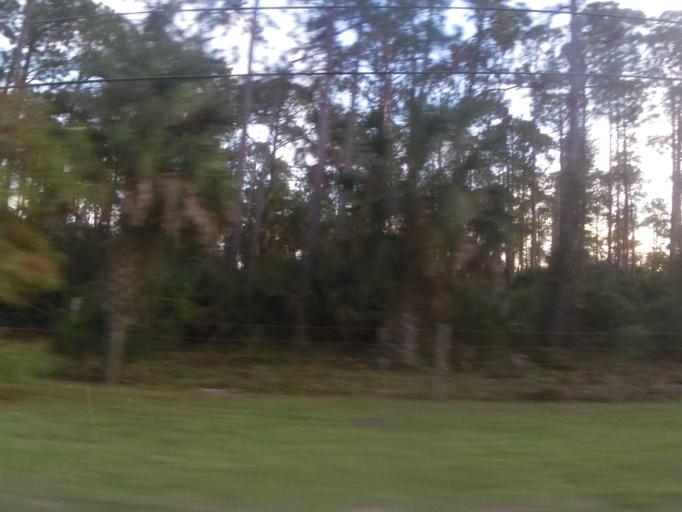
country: US
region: Florida
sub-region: Saint Johns County
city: Palm Valley
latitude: 30.1336
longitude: -81.3830
